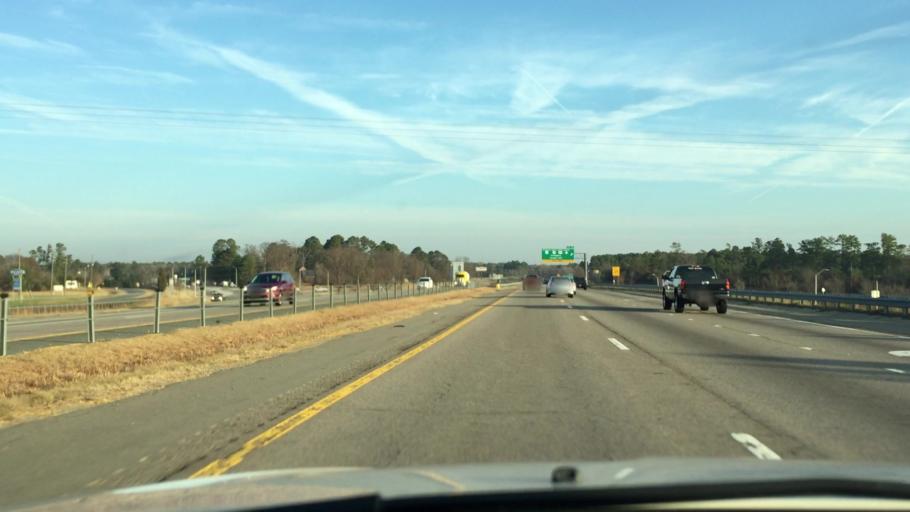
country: US
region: North Carolina
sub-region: Lee County
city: Sanford
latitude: 35.5214
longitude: -79.1844
